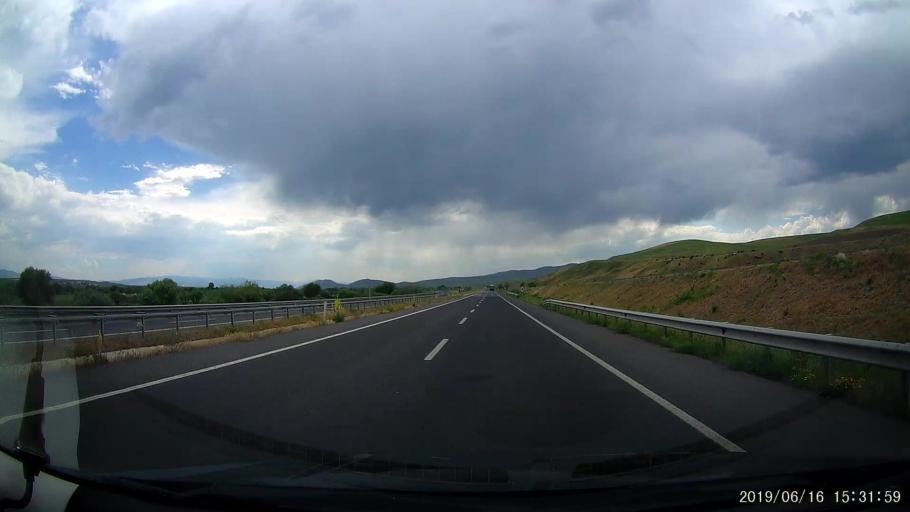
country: TR
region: Erzurum
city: Horasan
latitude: 40.0302
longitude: 42.0619
